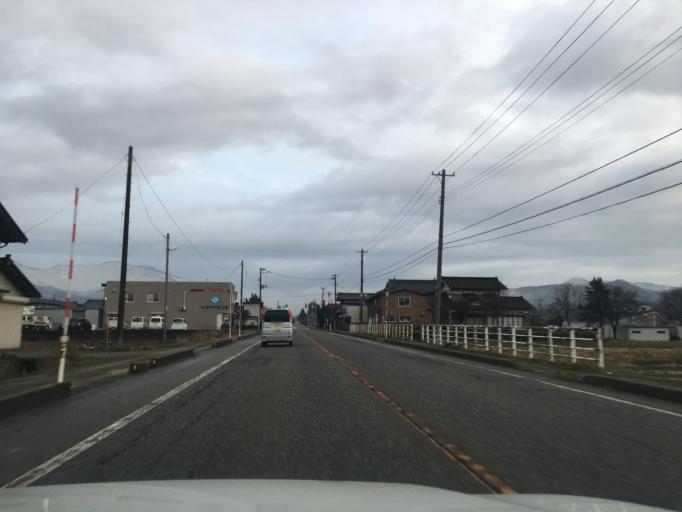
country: JP
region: Niigata
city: Murakami
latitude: 38.3247
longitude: 139.5556
